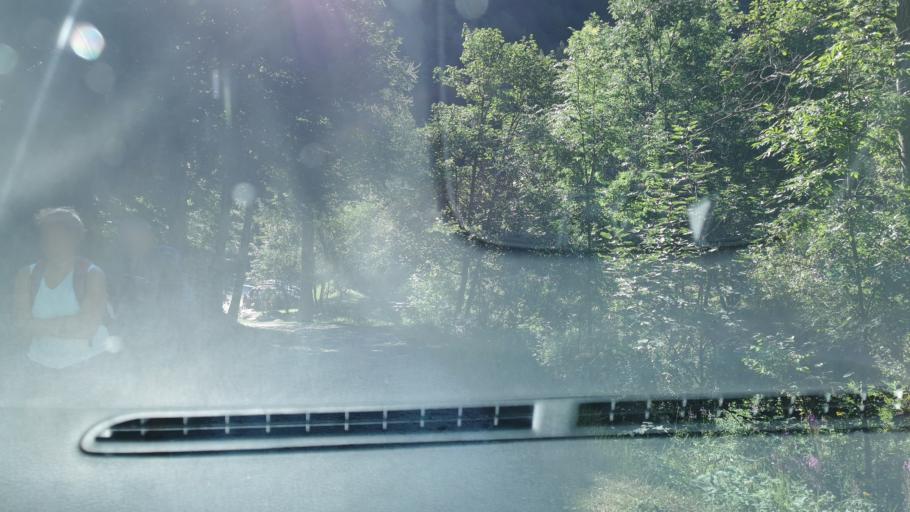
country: IT
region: Piedmont
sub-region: Provincia di Cuneo
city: Demonte
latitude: 44.2048
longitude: 7.2686
